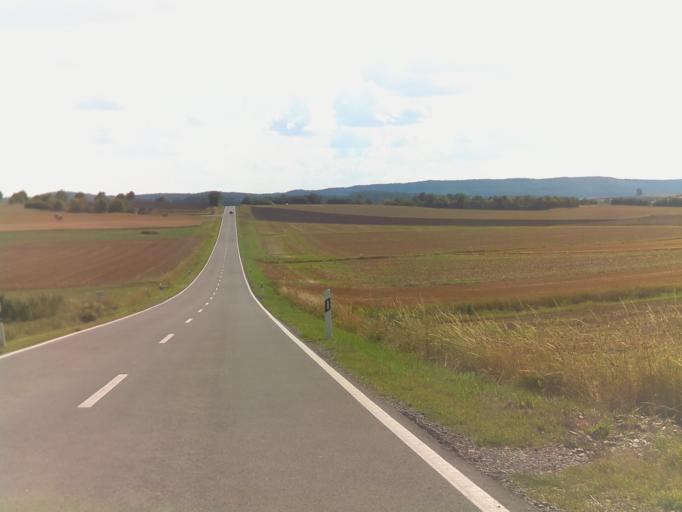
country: DE
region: Bavaria
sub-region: Regierungsbezirk Unterfranken
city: Trappstadt
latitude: 50.2745
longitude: 10.5496
